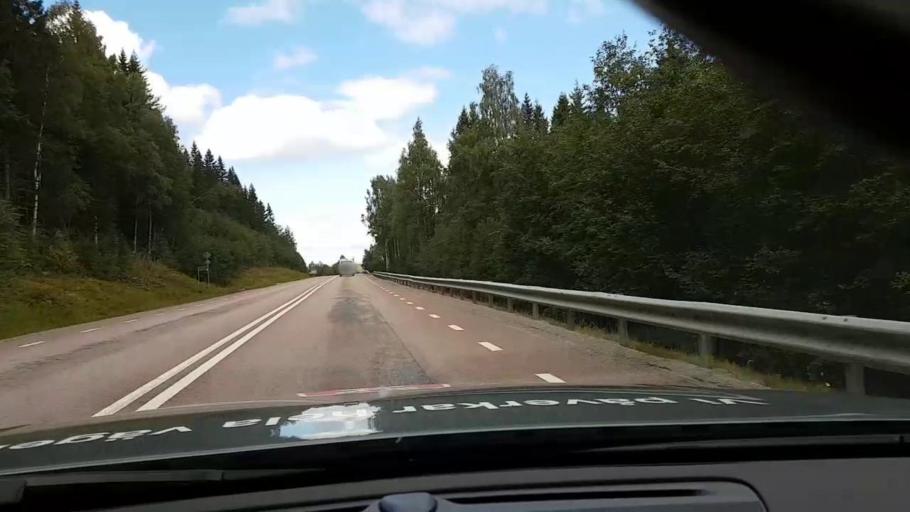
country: SE
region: Vaesternorrland
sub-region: OErnskoeldsviks Kommun
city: Bjasta
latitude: 63.3604
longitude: 18.4656
